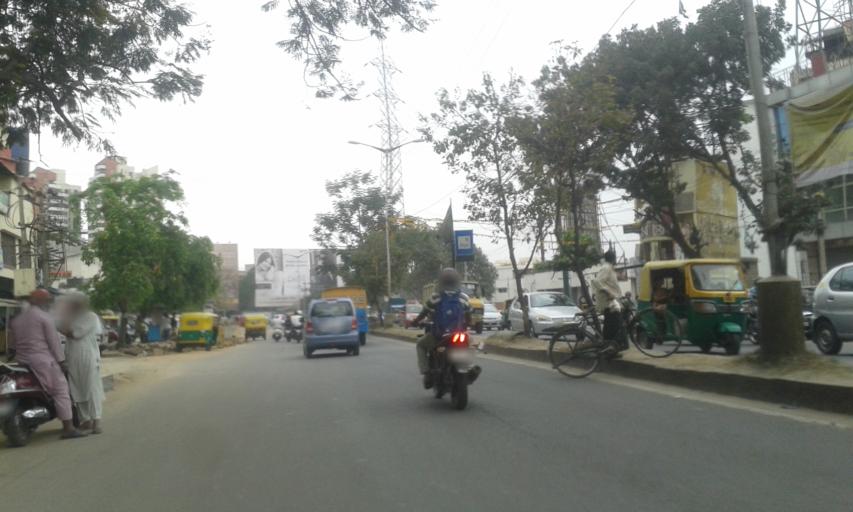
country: IN
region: Karnataka
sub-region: Bangalore Urban
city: Bangalore
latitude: 12.9076
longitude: 77.5712
